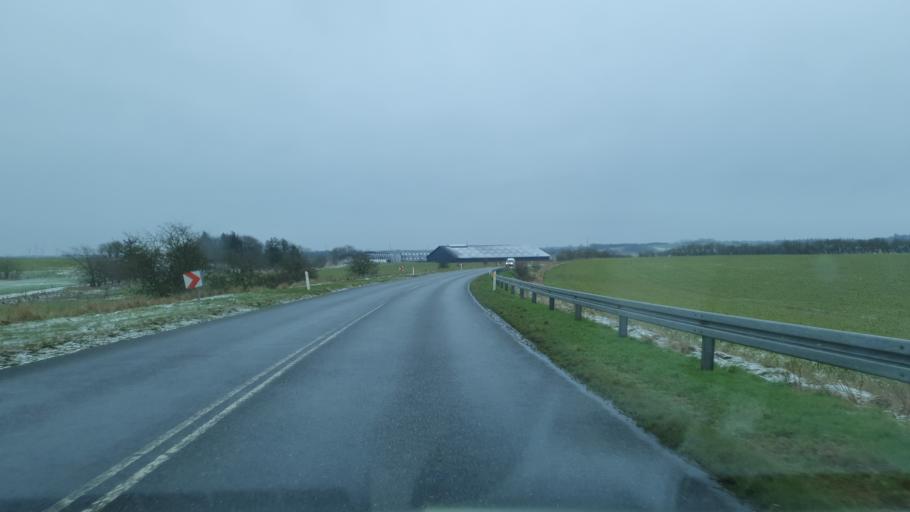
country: DK
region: North Denmark
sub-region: Jammerbugt Kommune
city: Brovst
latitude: 57.1256
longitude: 9.4863
